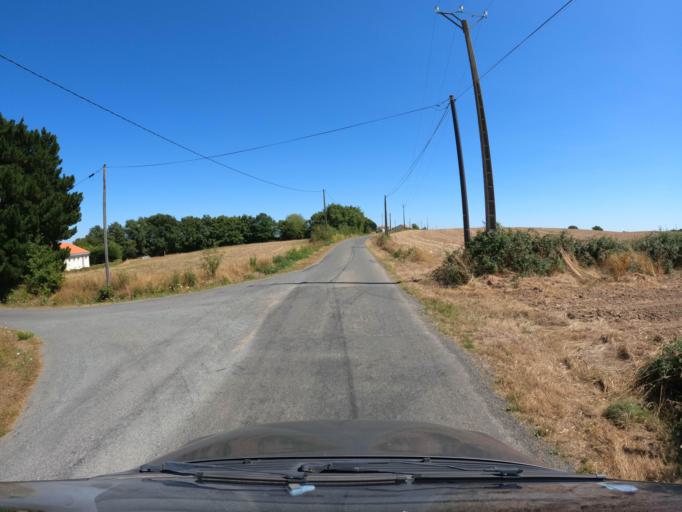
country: FR
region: Pays de la Loire
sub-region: Departement de Maine-et-Loire
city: Saint-Christophe-du-Bois
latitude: 47.0468
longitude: -0.9584
